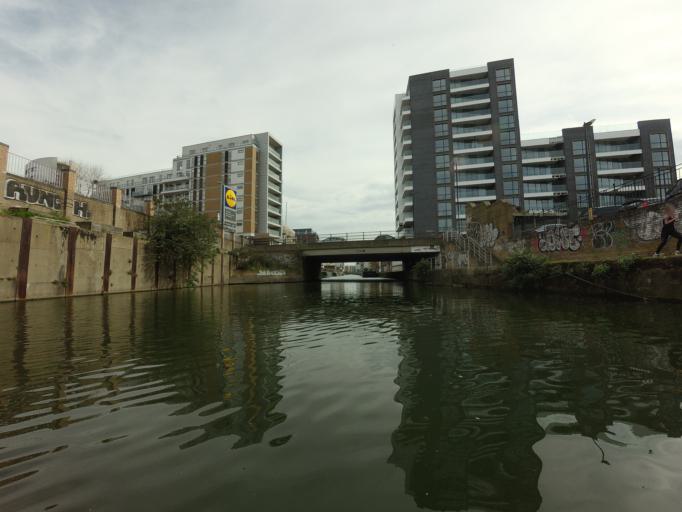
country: GB
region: England
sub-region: Greater London
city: Poplar
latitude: 51.5138
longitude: -0.0287
